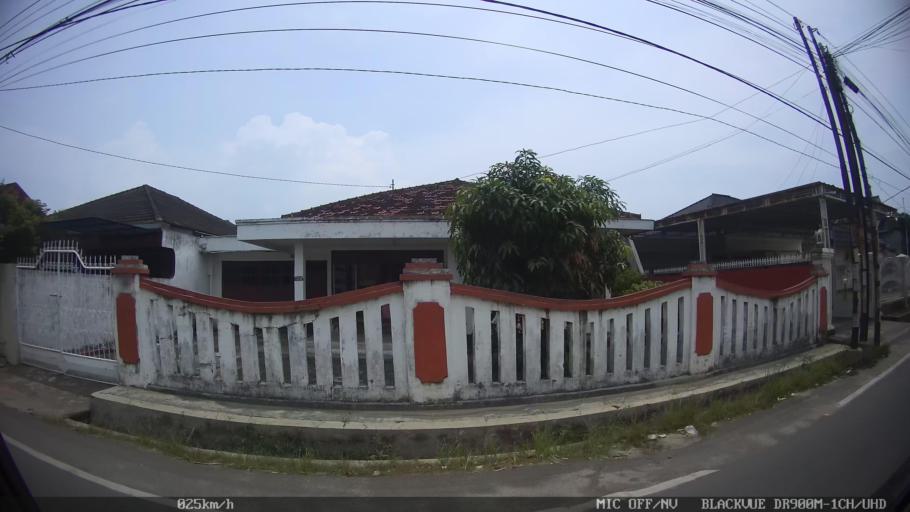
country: ID
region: Lampung
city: Bandarlampung
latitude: -5.4175
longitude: 105.2736
